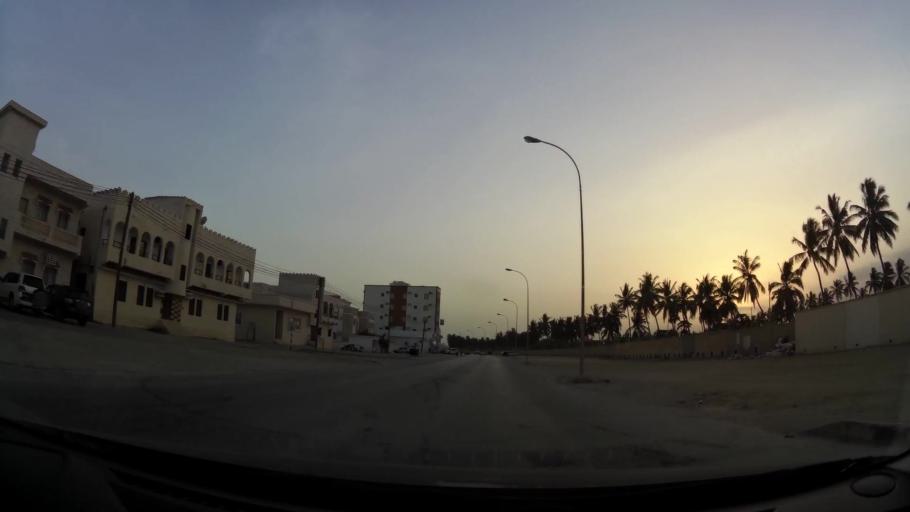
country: OM
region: Zufar
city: Salalah
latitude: 17.0231
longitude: 54.1278
